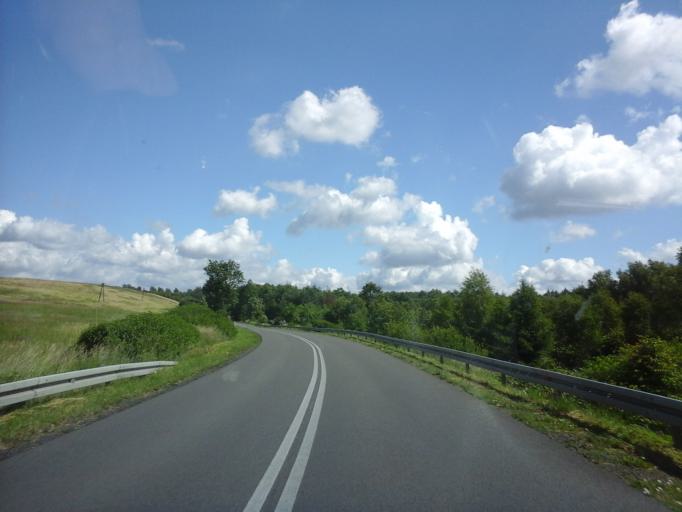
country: PL
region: West Pomeranian Voivodeship
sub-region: Powiat lobeski
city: Wegorzyno
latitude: 53.5611
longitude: 15.5724
